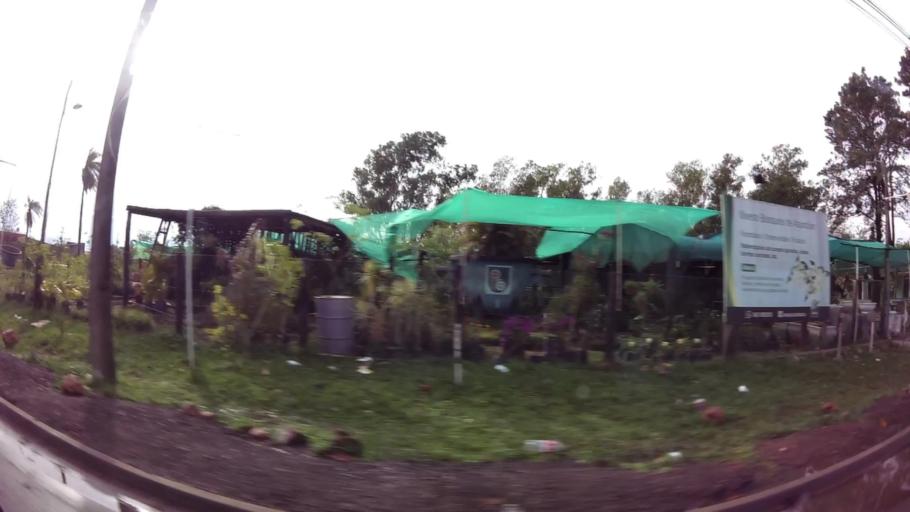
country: PY
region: Central
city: Limpio
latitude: -25.1866
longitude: -57.4955
